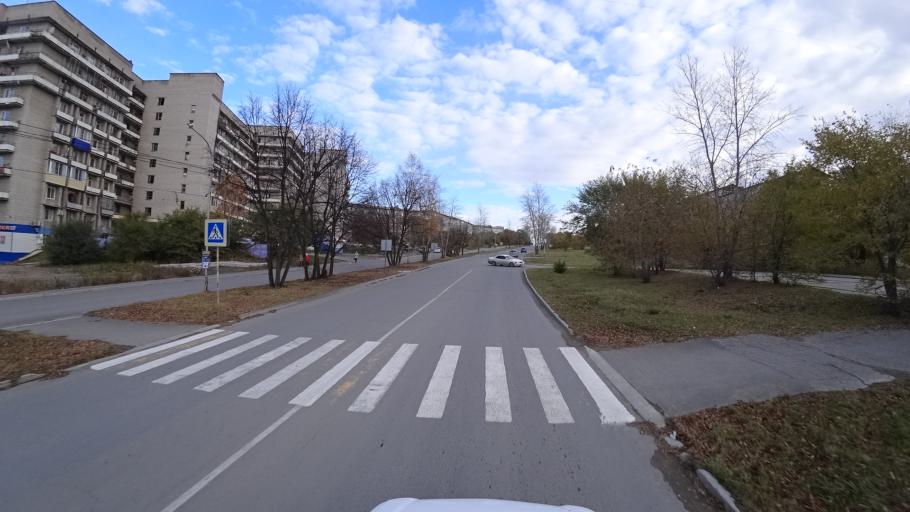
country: RU
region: Khabarovsk Krai
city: Amursk
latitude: 50.2388
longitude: 136.9115
